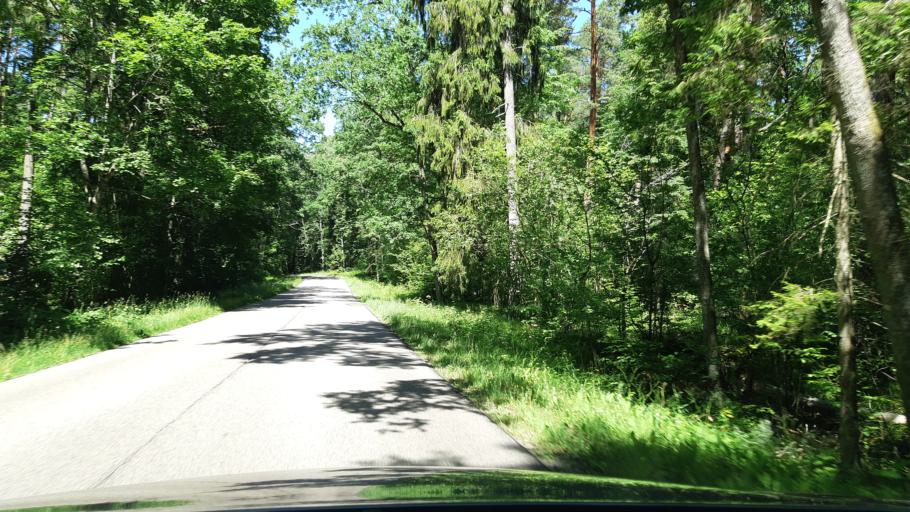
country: PL
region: Warmian-Masurian Voivodeship
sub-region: Powiat mragowski
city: Mikolajki
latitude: 53.7501
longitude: 21.5024
